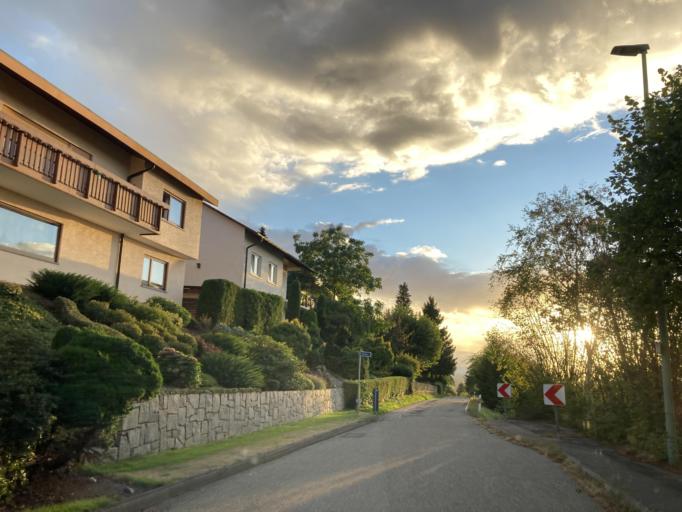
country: DE
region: Baden-Wuerttemberg
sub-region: Freiburg Region
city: Lauf
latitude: 48.6693
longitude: 8.1466
